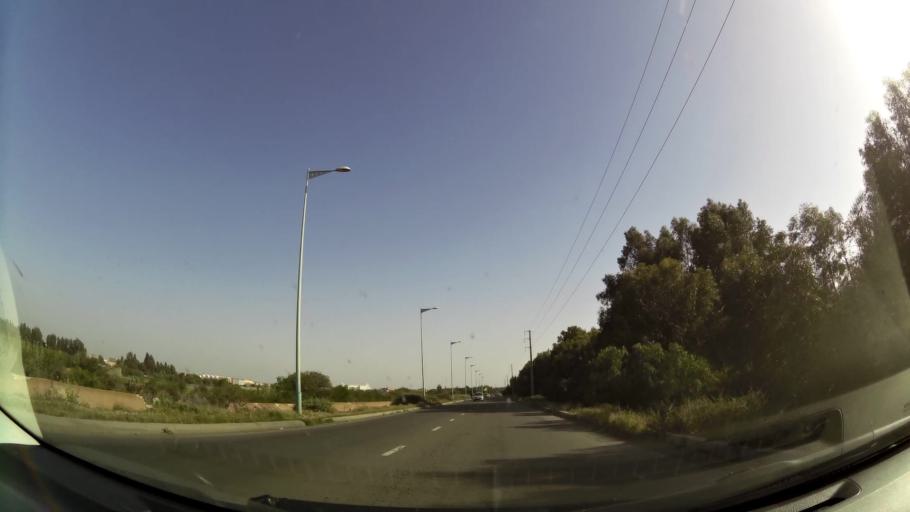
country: MA
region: Souss-Massa-Draa
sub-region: Inezgane-Ait Mellou
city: Inezgane
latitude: 30.3561
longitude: -9.5060
